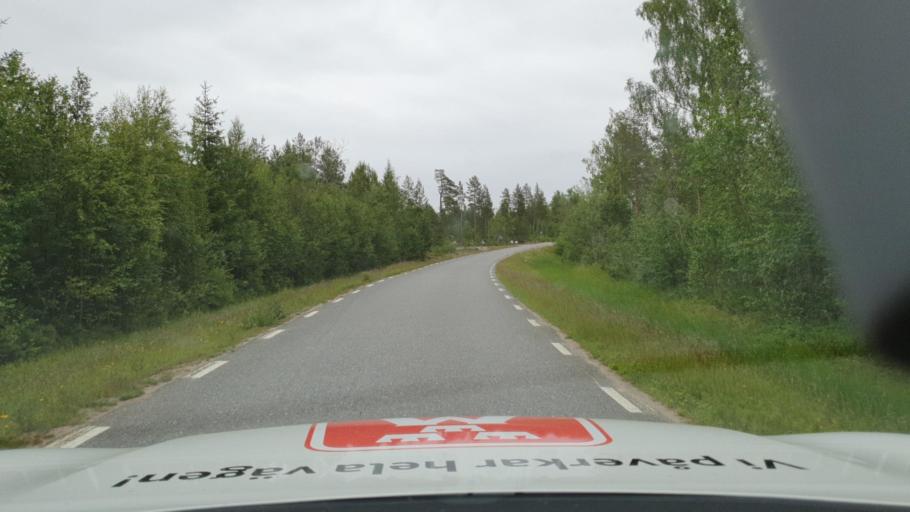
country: SE
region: Vaesterbotten
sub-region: Nordmalings Kommun
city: Nordmaling
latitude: 63.4329
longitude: 19.4850
